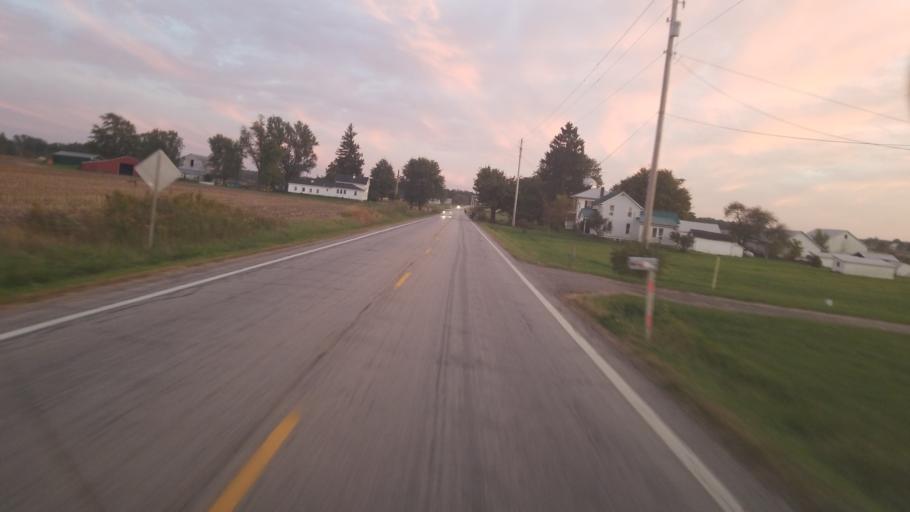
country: US
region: Ohio
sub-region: Ashtabula County
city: Andover
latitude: 41.6679
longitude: -80.6676
